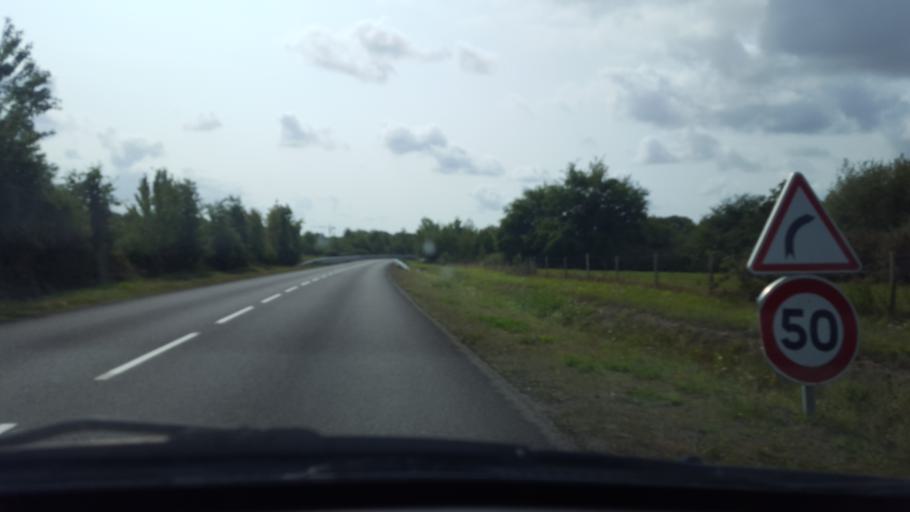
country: FR
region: Pays de la Loire
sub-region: Departement de la Loire-Atlantique
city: Paulx
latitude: 46.9968
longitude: -1.7458
